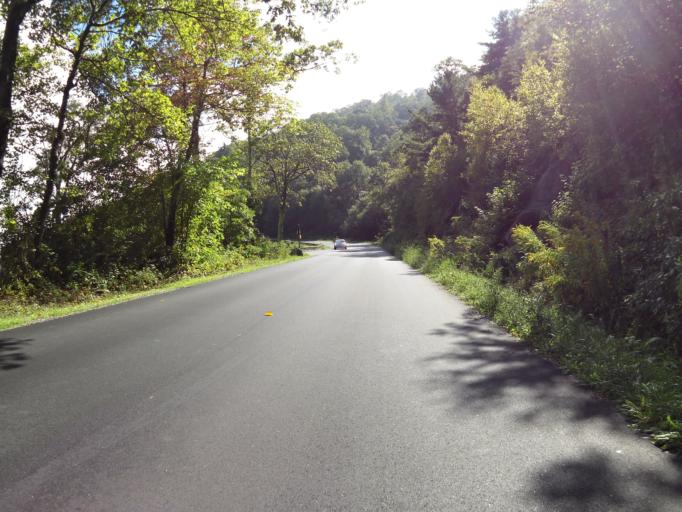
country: US
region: Virginia
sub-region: Page County
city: Luray
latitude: 38.6517
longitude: -78.3117
